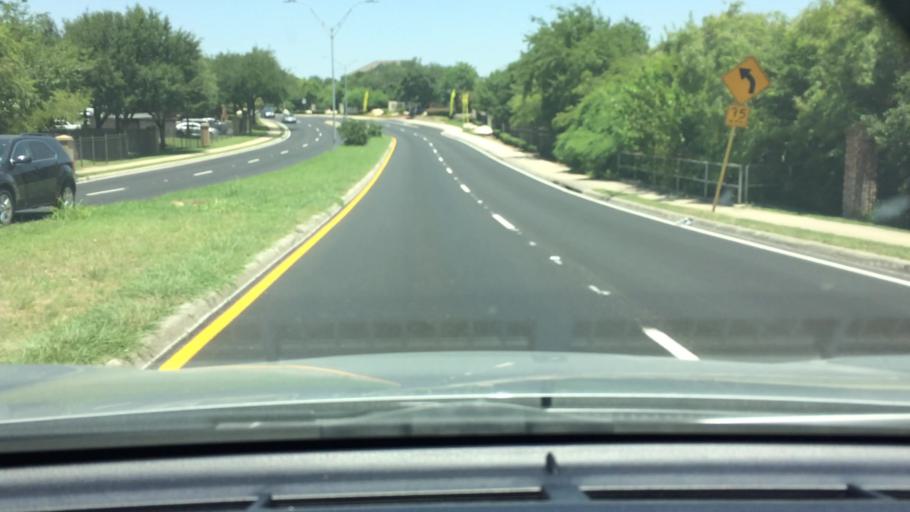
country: US
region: Texas
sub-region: Bexar County
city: Shavano Park
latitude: 29.5563
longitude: -98.5741
